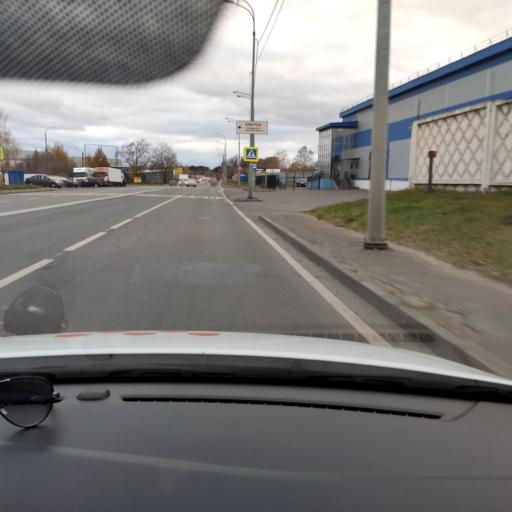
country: RU
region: Tatarstan
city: Staroye Arakchino
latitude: 55.8373
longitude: 49.0380
